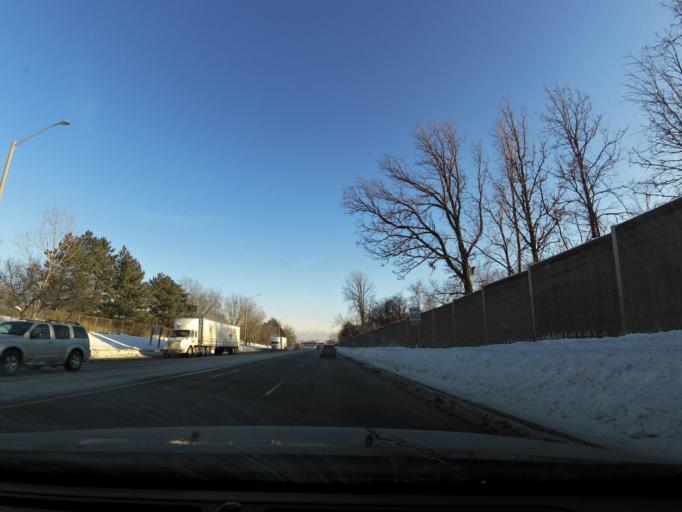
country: CA
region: Ontario
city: Etobicoke
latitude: 43.7354
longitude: -79.6370
